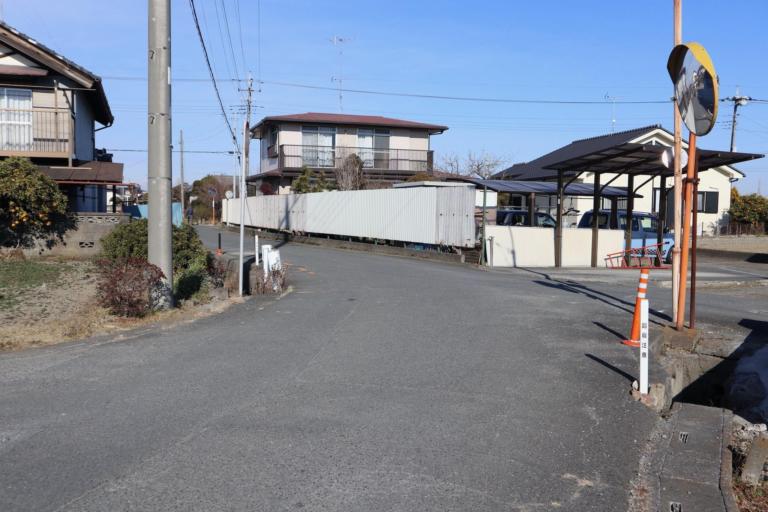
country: JP
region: Saitama
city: Fukiage-fujimi
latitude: 36.0927
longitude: 139.4458
